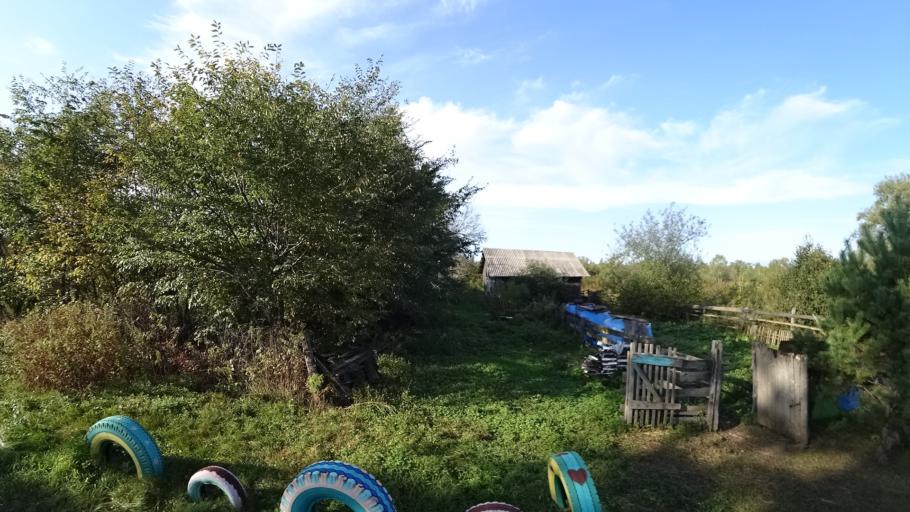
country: RU
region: Amur
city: Arkhara
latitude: 49.3496
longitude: 130.1201
